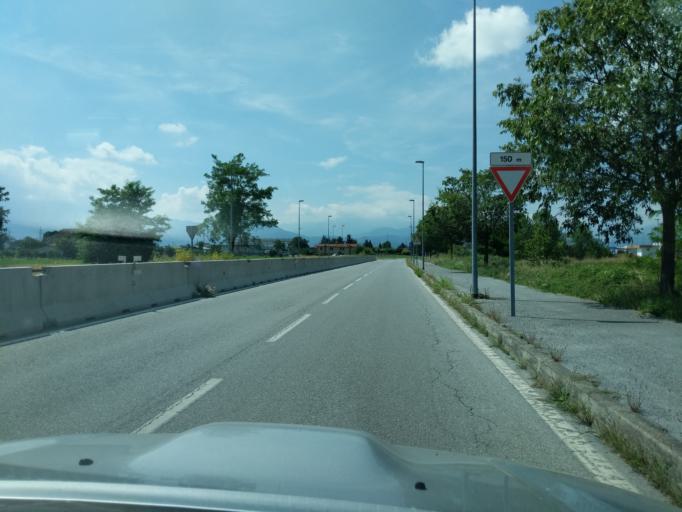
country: IT
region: Piedmont
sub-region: Provincia di Cuneo
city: Cuneo
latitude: 44.3947
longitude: 7.5874
